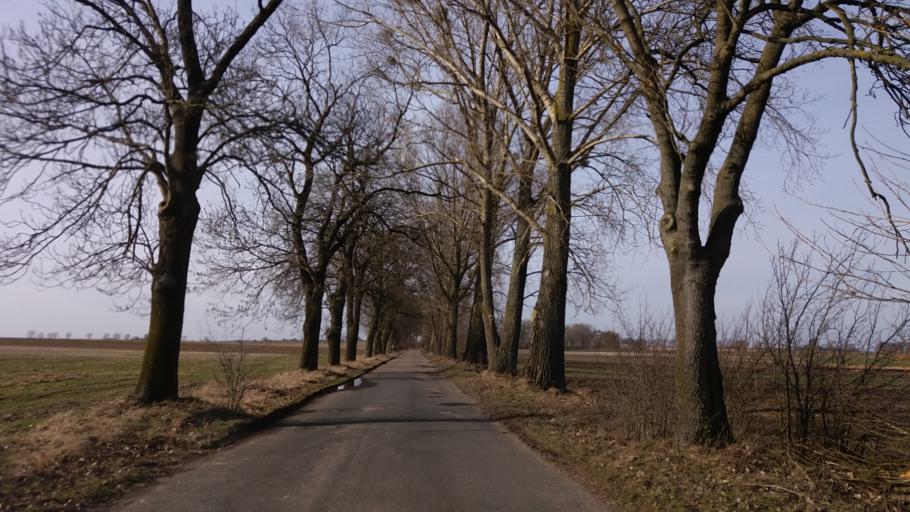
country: PL
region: West Pomeranian Voivodeship
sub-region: Powiat choszczenski
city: Choszczno
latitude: 53.1117
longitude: 15.4032
